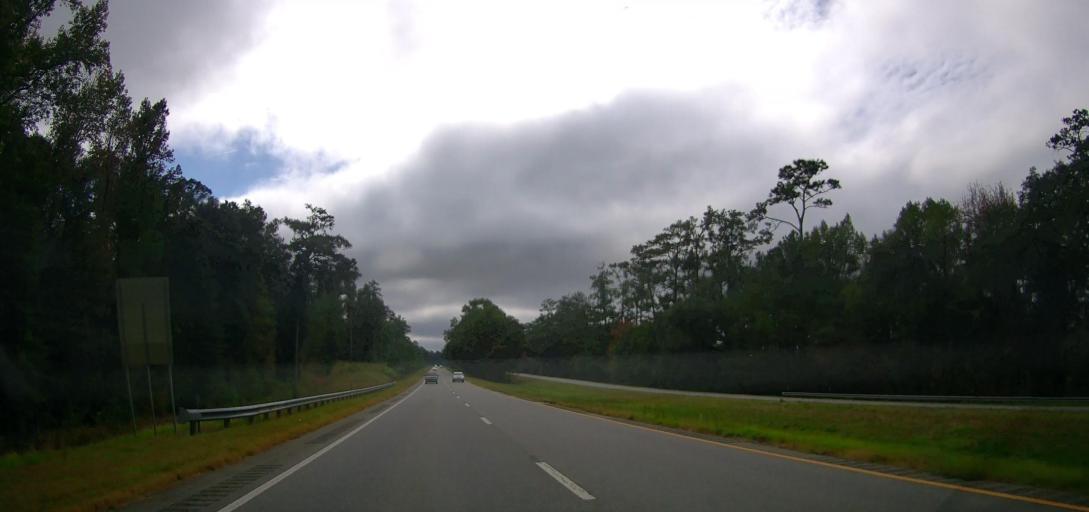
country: US
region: Georgia
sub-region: Grady County
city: Cairo
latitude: 30.6954
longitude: -84.1485
